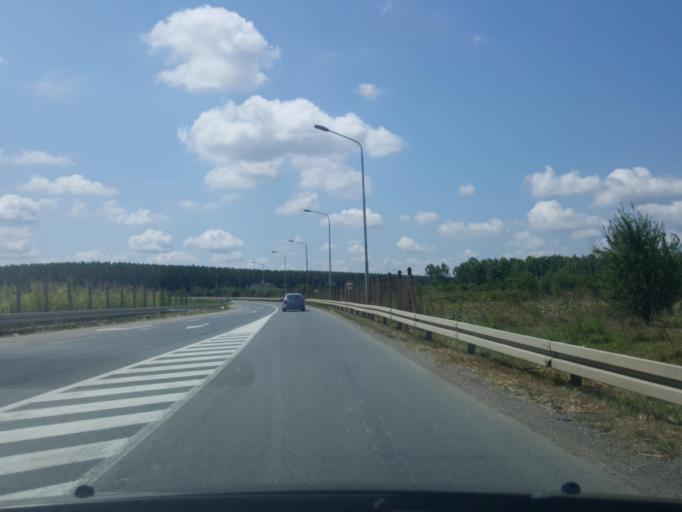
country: RS
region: Autonomna Pokrajina Vojvodina
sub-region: Sremski Okrug
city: Sremska Mitrovica
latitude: 44.9669
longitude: 19.6331
